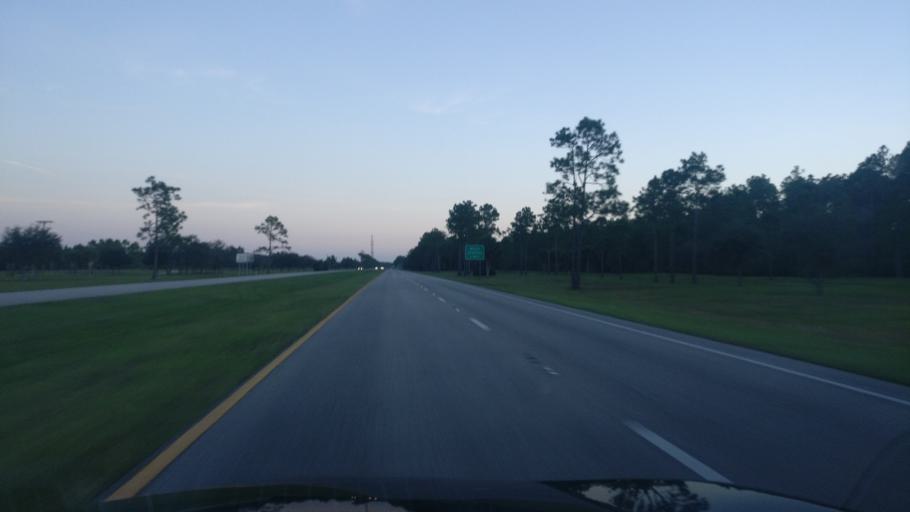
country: US
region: Florida
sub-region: Flagler County
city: Palm Coast
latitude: 29.5740
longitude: -81.2754
